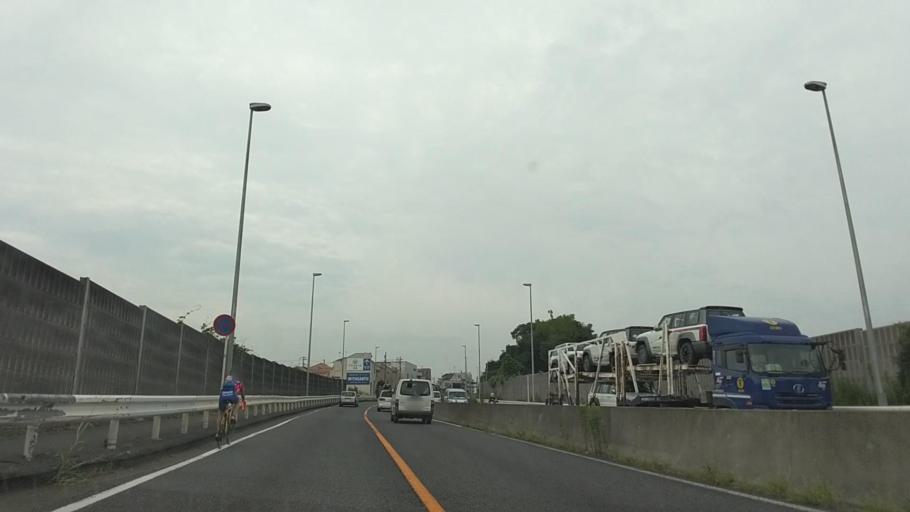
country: JP
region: Kanagawa
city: Fujisawa
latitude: 35.4105
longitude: 139.5311
